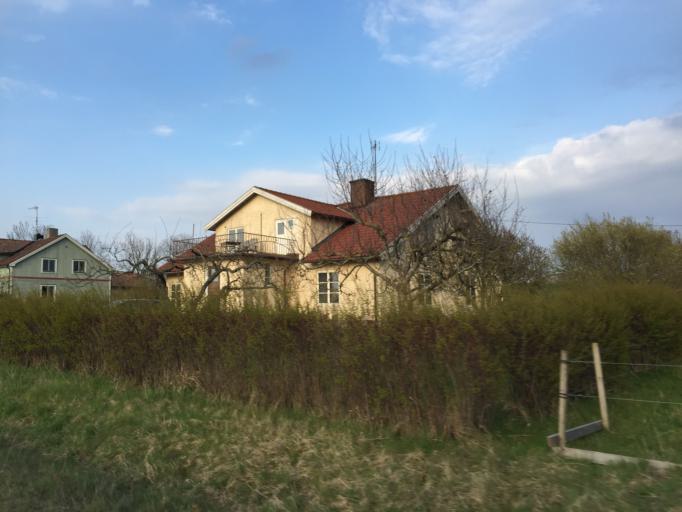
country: SE
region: Stockholm
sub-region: Sodertalje Kommun
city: Pershagen
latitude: 59.0748
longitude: 17.6062
